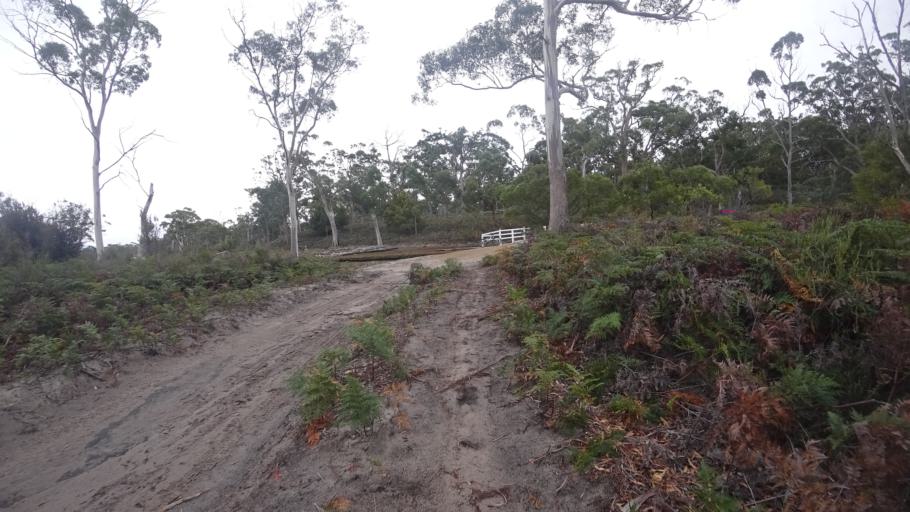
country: AU
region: Tasmania
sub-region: Sorell
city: Sorell
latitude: -42.6535
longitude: 148.0455
